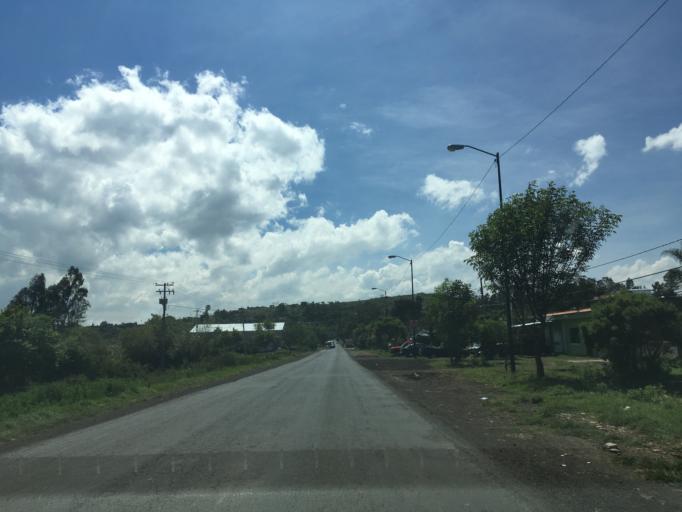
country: MX
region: Michoacan
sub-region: Morelia
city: San Antonio
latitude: 19.6753
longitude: -101.2790
